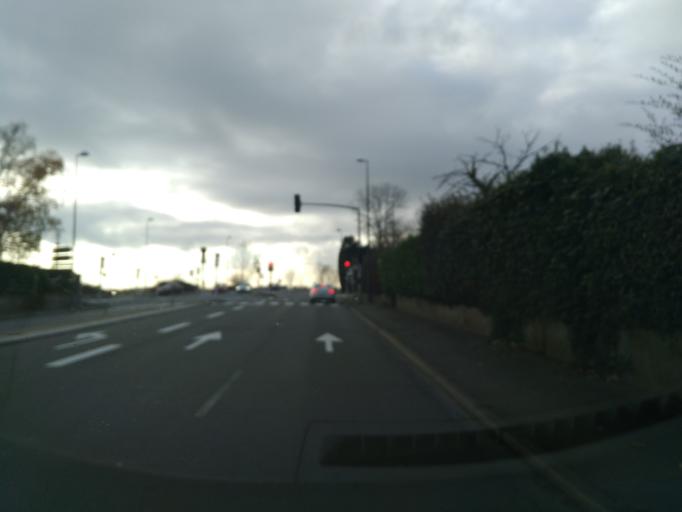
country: FR
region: Ile-de-France
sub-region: Departement des Yvelines
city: Guyancourt
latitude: 48.7751
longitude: 2.0910
